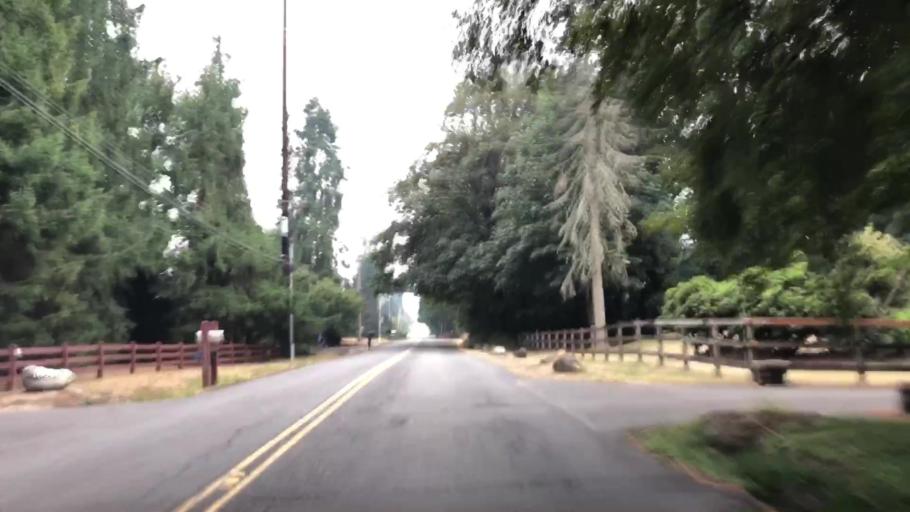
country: US
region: Washington
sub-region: King County
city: Cottage Lake
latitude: 47.7415
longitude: -122.1152
